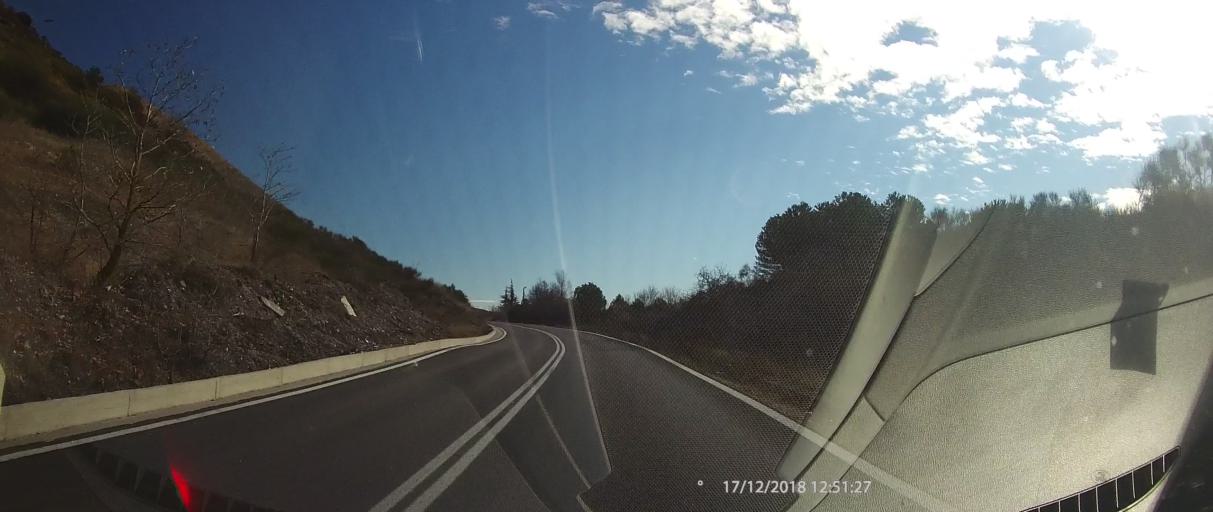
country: GR
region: Thessaly
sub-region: Trikala
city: Kastraki
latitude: 39.7661
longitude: 21.4648
